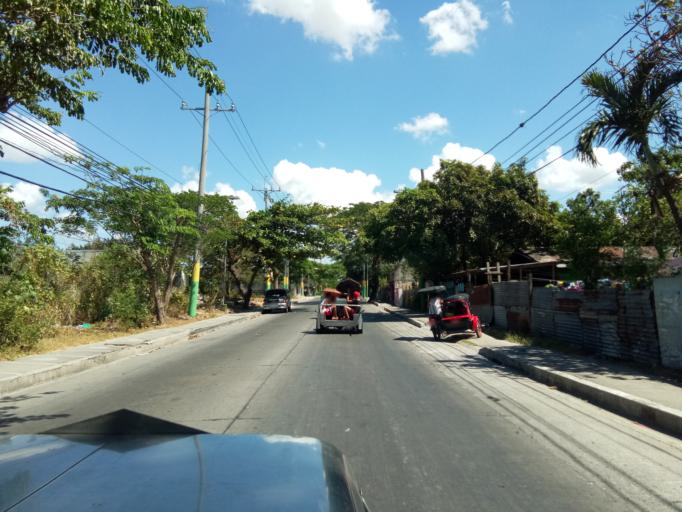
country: PH
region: Calabarzon
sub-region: Province of Cavite
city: Dasmarinas
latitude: 14.3475
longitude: 120.9455
